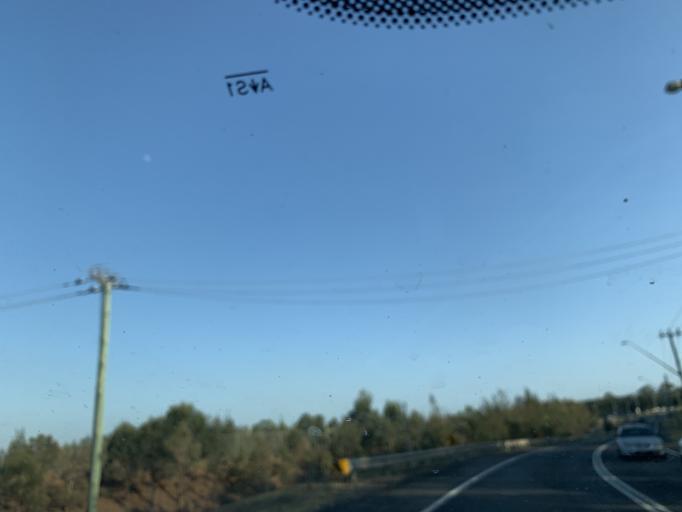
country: AU
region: New South Wales
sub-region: Fairfield
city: Horsley Park
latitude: -33.8206
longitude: 150.8670
